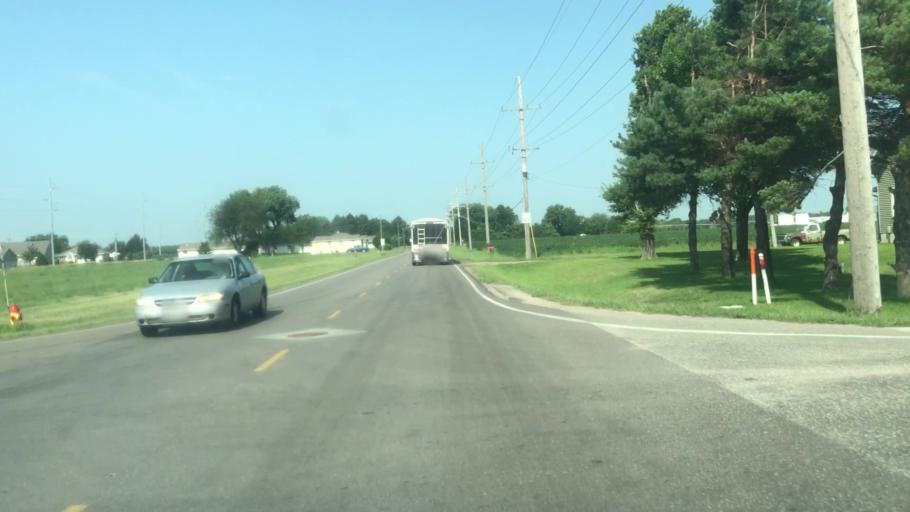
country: US
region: Nebraska
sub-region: Hall County
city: Grand Island
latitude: 40.9455
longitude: -98.3206
